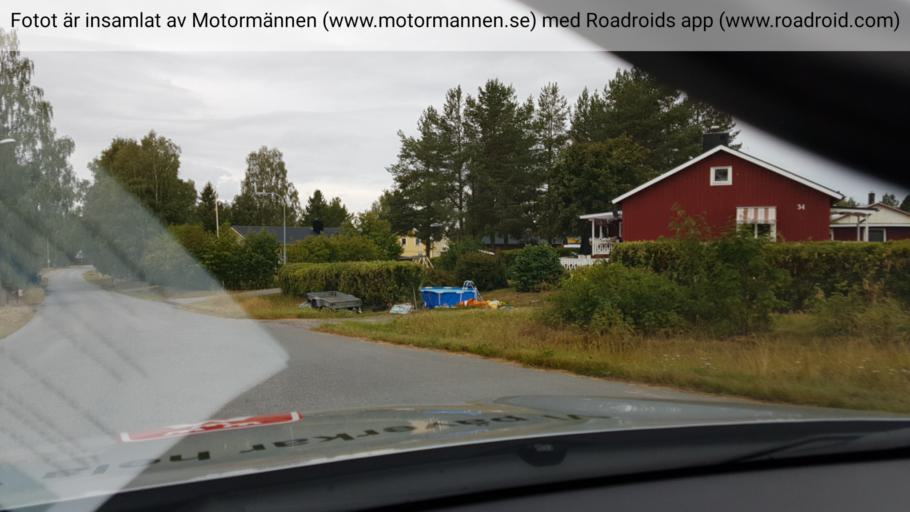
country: SE
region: Norrbotten
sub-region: Bodens Kommun
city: Boden
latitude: 65.8138
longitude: 21.5773
